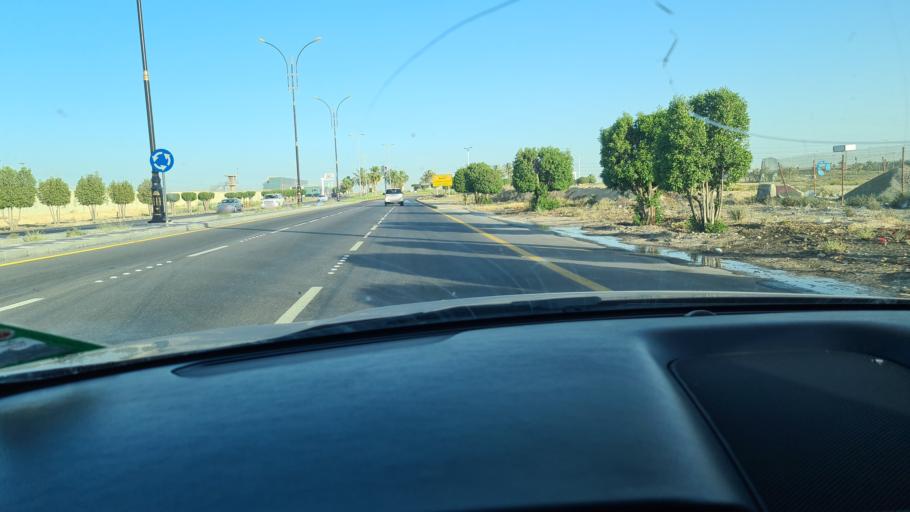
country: SA
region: Eastern Province
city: Al Jubayl
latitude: 26.9293
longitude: 49.7101
